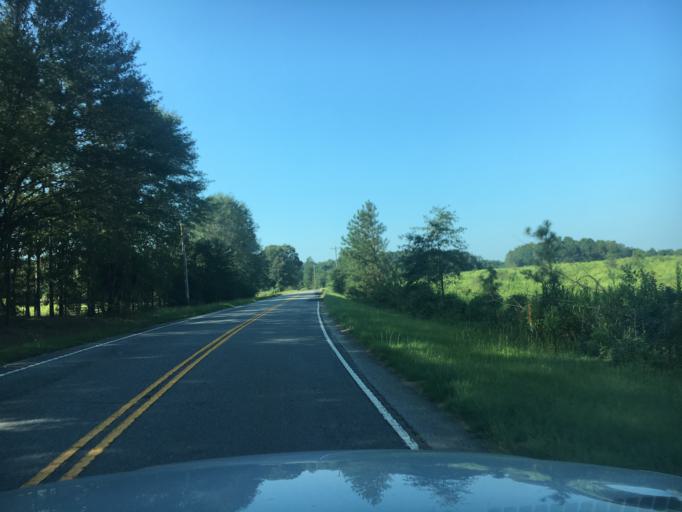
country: US
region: South Carolina
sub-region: Anderson County
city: Williamston
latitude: 34.6288
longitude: -82.3482
